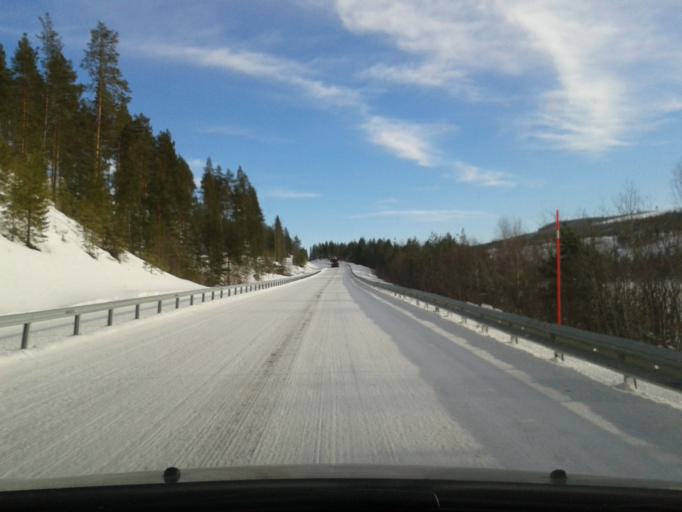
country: SE
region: Vaesterbotten
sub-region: Asele Kommun
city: Asele
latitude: 64.3188
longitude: 17.1221
